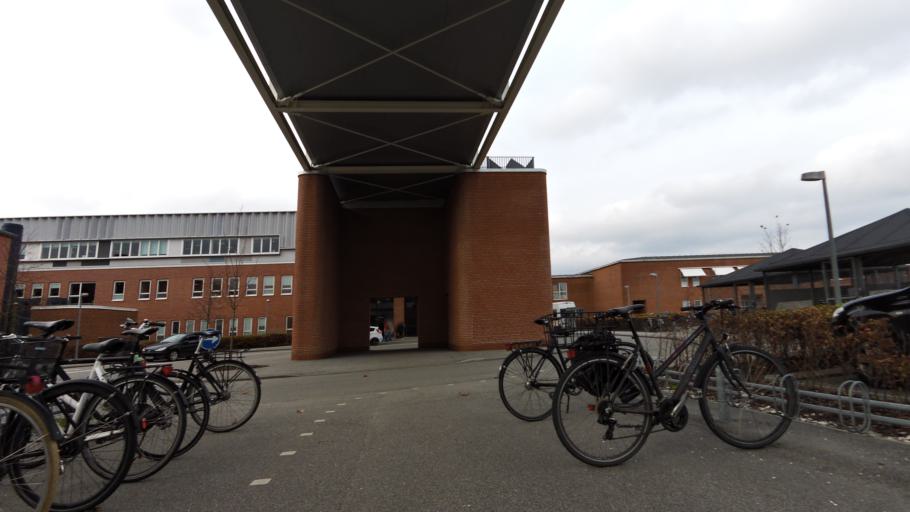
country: DK
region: Central Jutland
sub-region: Arhus Kommune
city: Arhus
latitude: 56.1885
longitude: 10.1744
